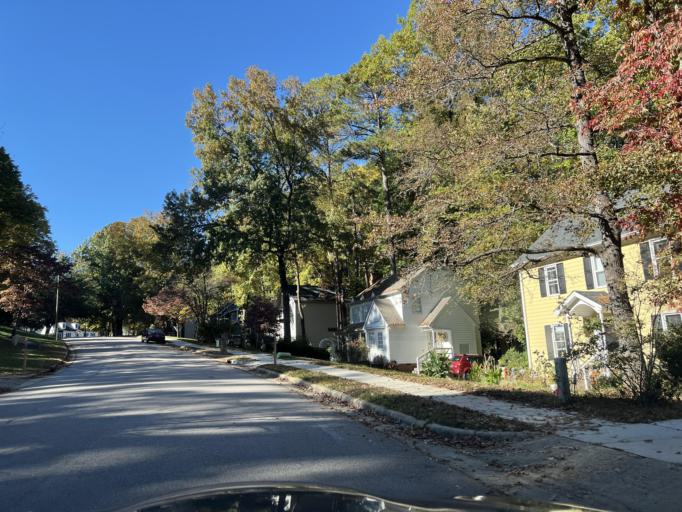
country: US
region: North Carolina
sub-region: Wake County
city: West Raleigh
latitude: 35.8910
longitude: -78.6457
